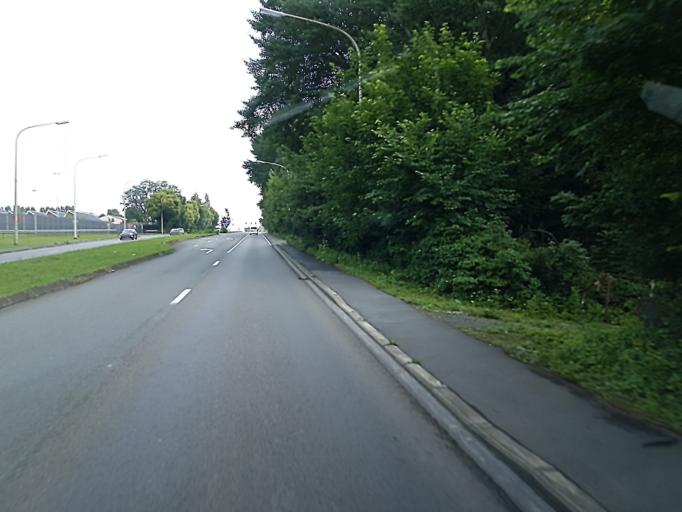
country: BE
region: Wallonia
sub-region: Province du Hainaut
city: Mons
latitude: 50.4945
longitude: 3.9778
